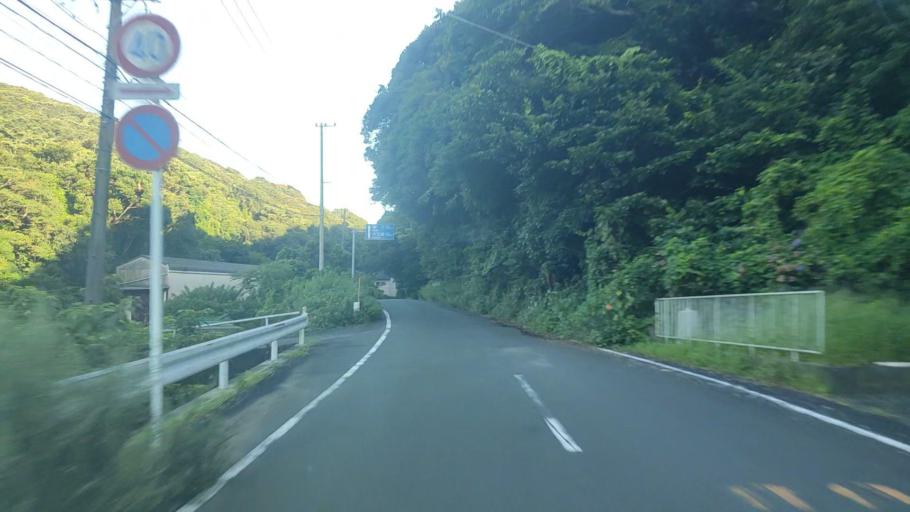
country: JP
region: Mie
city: Ise
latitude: 34.2720
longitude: 136.7655
